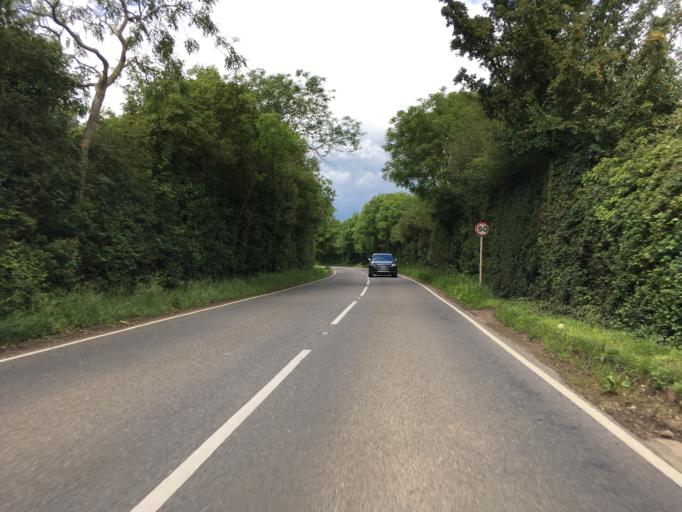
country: GB
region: England
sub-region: Northamptonshire
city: Brackley
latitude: 52.0763
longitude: -1.1260
